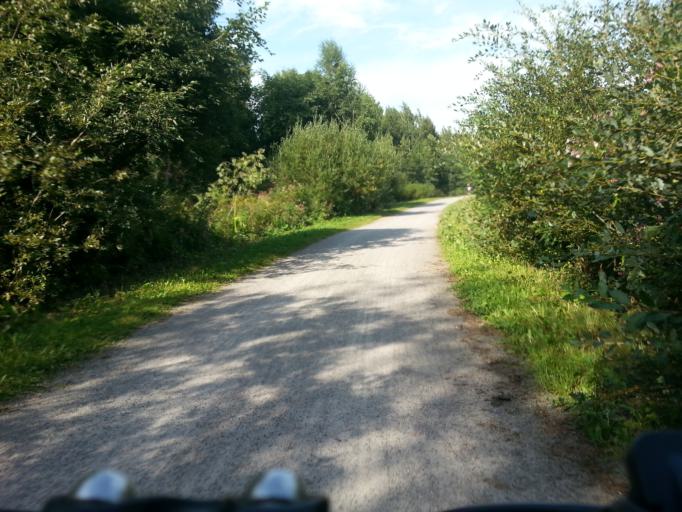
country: FI
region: Uusimaa
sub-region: Helsinki
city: Vantaa
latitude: 60.2348
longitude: 24.9913
